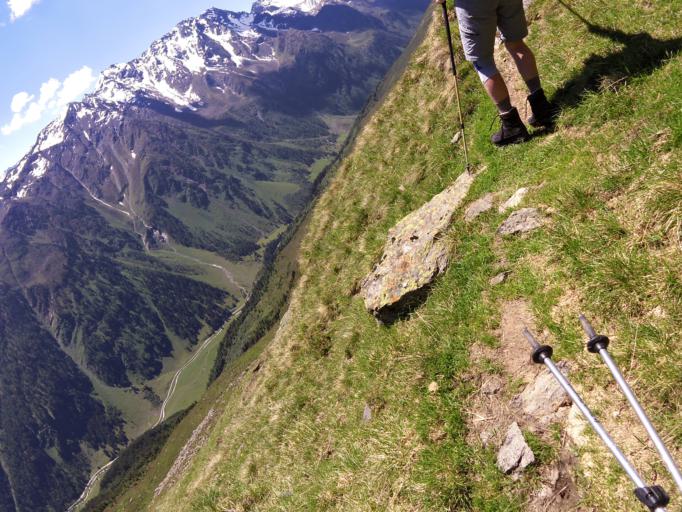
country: AT
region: Tyrol
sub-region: Politischer Bezirk Innsbruck Land
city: Sellrain
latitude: 47.1281
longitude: 11.2236
